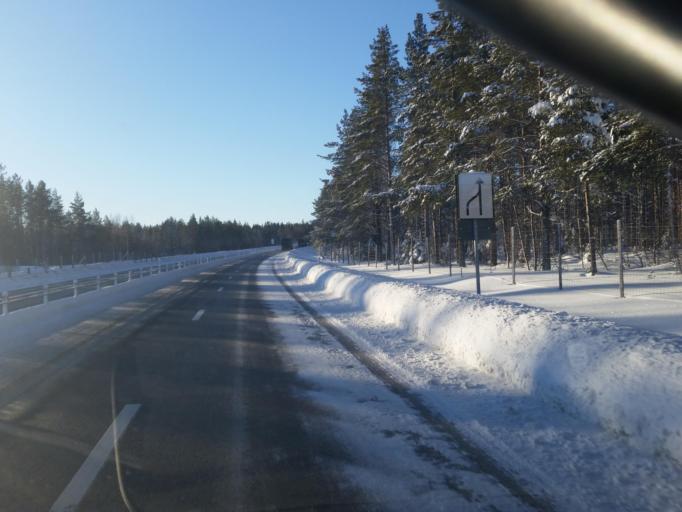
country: SE
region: Norrbotten
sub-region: Pitea Kommun
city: Pitea
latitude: 65.1117
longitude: 21.5239
